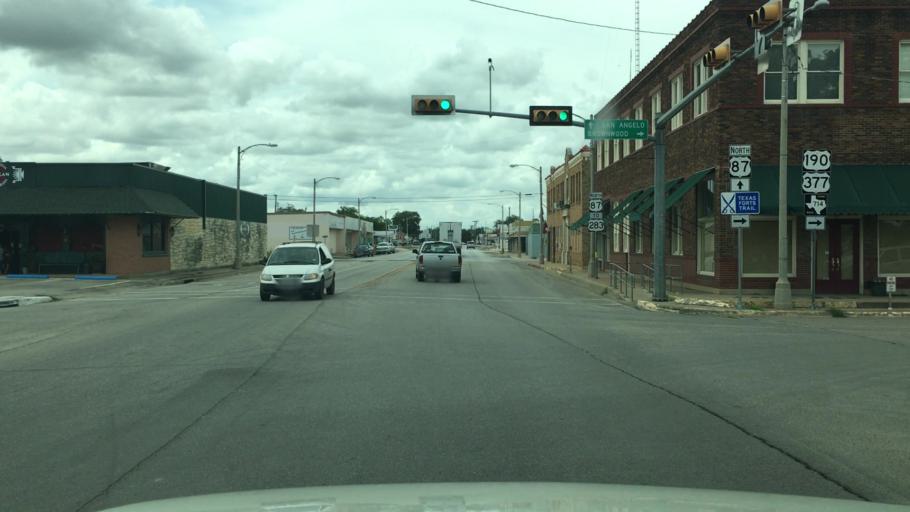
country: US
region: Texas
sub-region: McCulloch County
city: Brady
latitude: 31.1348
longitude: -99.3356
